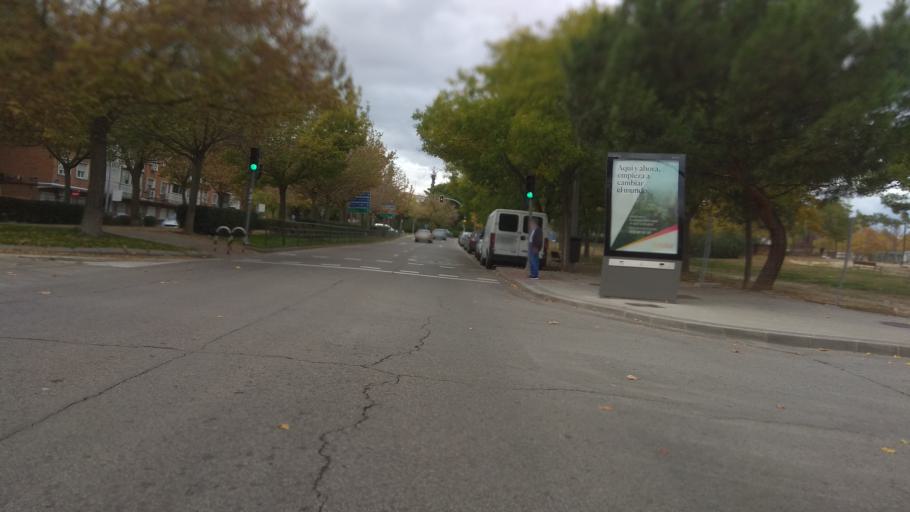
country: ES
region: Madrid
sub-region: Provincia de Madrid
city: Vicalvaro
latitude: 40.4090
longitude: -3.6079
